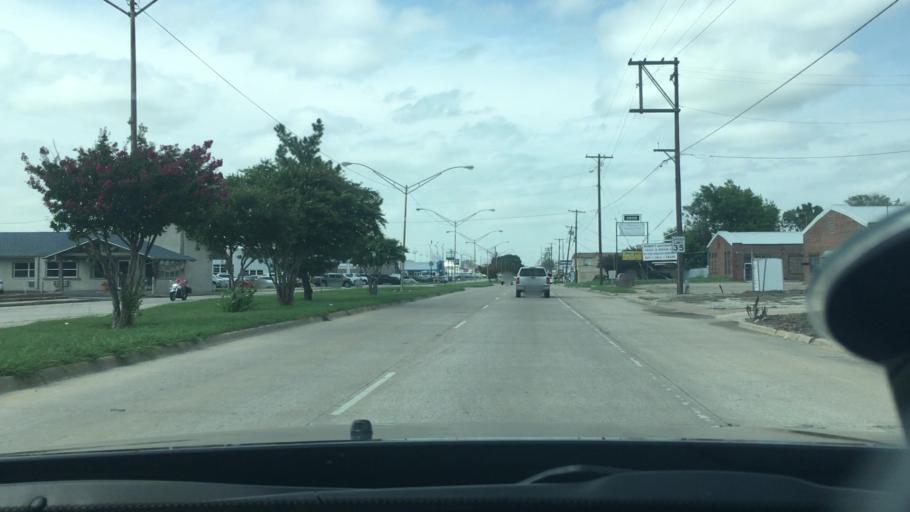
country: US
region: Oklahoma
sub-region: Pontotoc County
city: Ada
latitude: 34.7842
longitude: -96.6786
